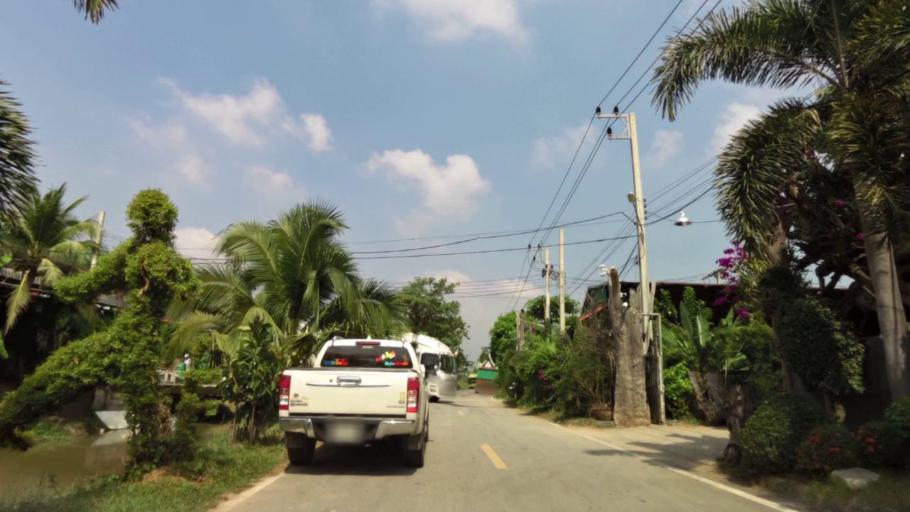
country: TH
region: Ang Thong
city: Pho Thong
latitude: 14.6094
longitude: 100.3976
